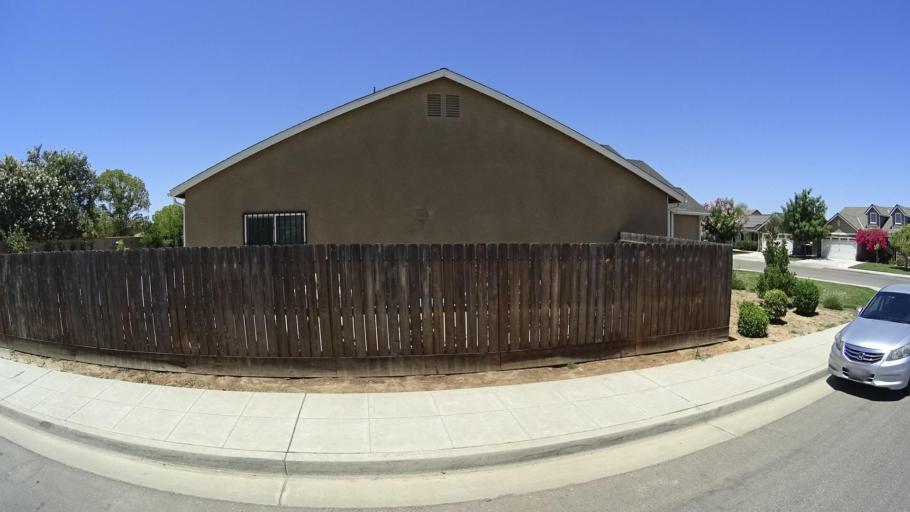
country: US
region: California
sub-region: Fresno County
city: Sunnyside
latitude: 36.7261
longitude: -119.6704
